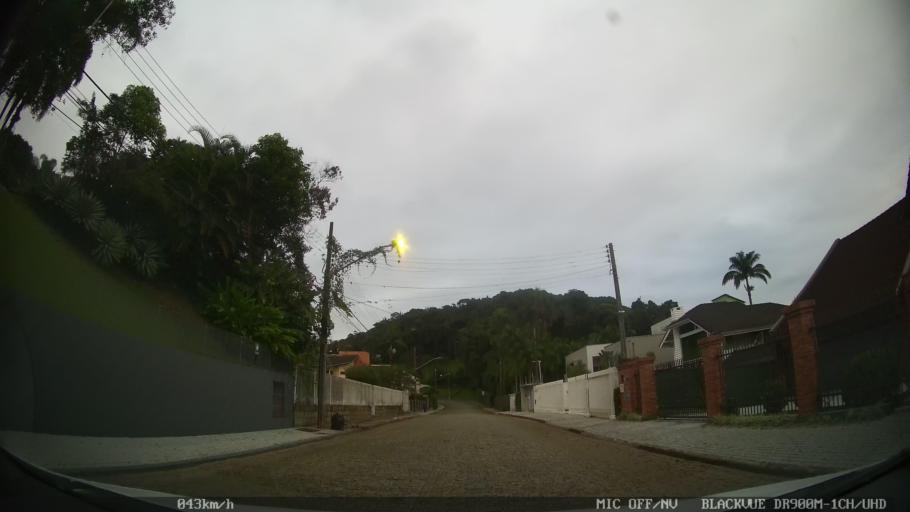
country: BR
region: Santa Catarina
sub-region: Joinville
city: Joinville
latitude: -26.2961
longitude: -48.8564
